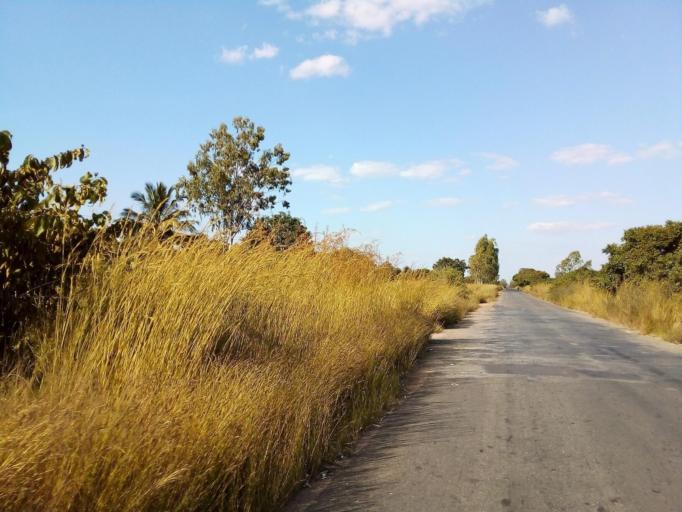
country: MZ
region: Zambezia
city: Quelimane
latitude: -17.5756
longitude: 36.6317
